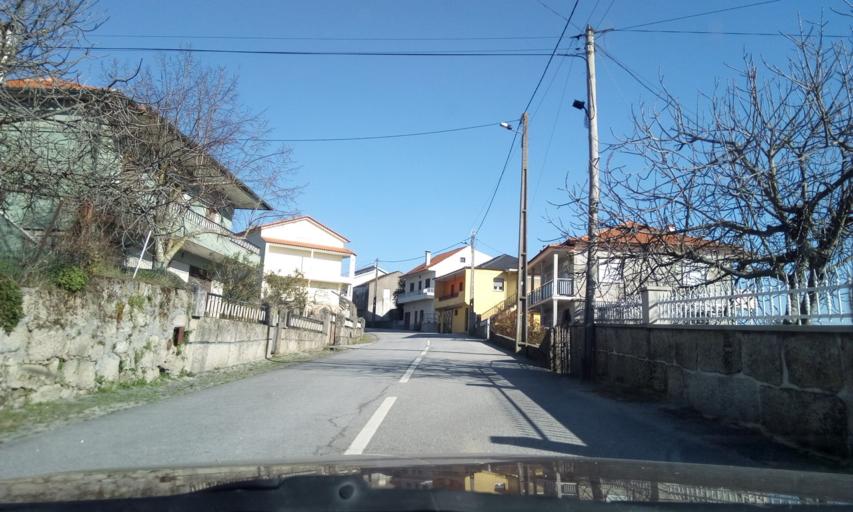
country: PT
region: Guarda
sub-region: Celorico da Beira
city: Celorico da Beira
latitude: 40.6551
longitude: -7.4643
